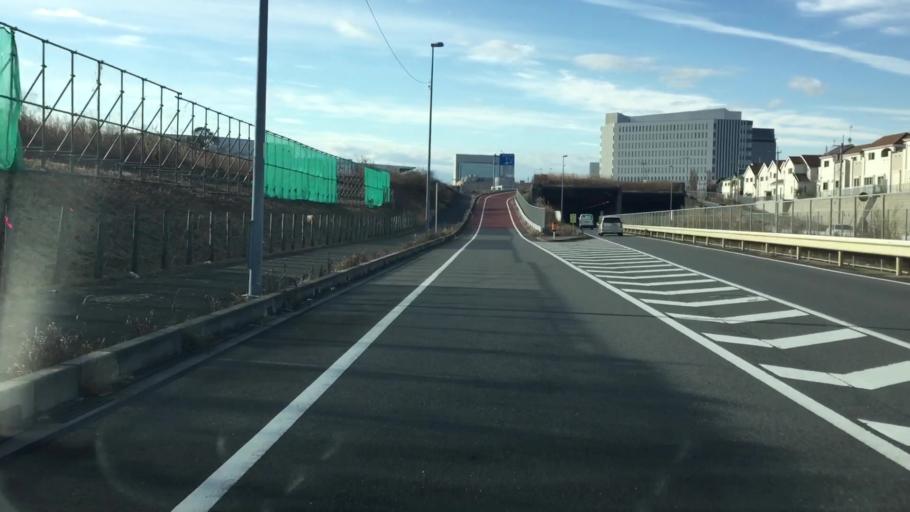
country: JP
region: Chiba
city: Shiroi
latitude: 35.8137
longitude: 140.1268
